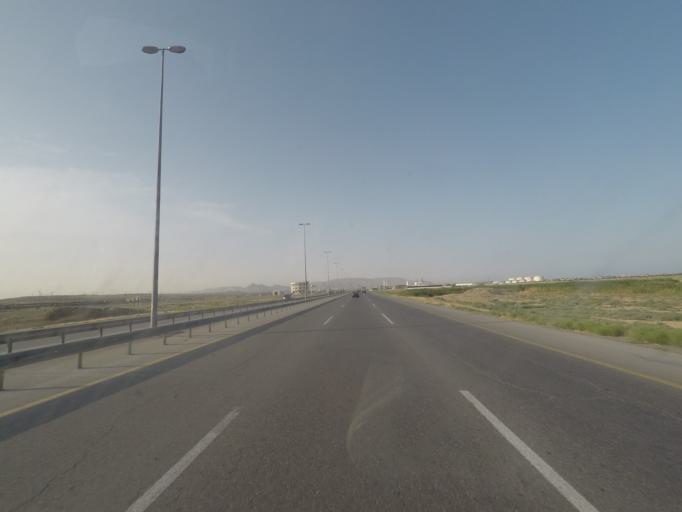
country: AZ
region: Baki
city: Qobustan
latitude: 40.1422
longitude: 49.4506
